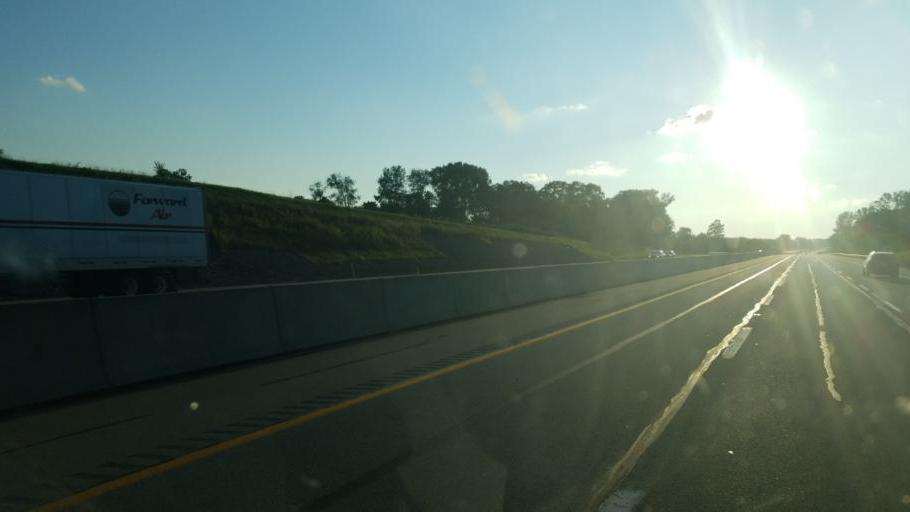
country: US
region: Pennsylvania
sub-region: Lawrence County
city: New Beaver
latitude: 40.8891
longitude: -80.4460
